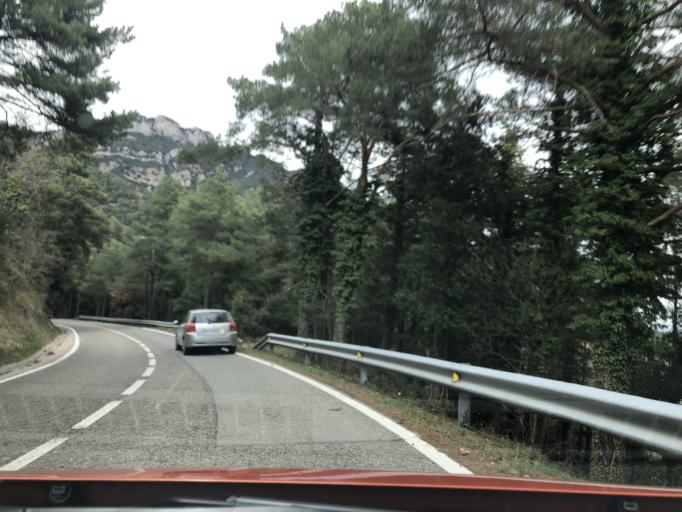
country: ES
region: Catalonia
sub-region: Provincia de Barcelona
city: Castellar del Riu
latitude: 42.0936
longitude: 1.7915
